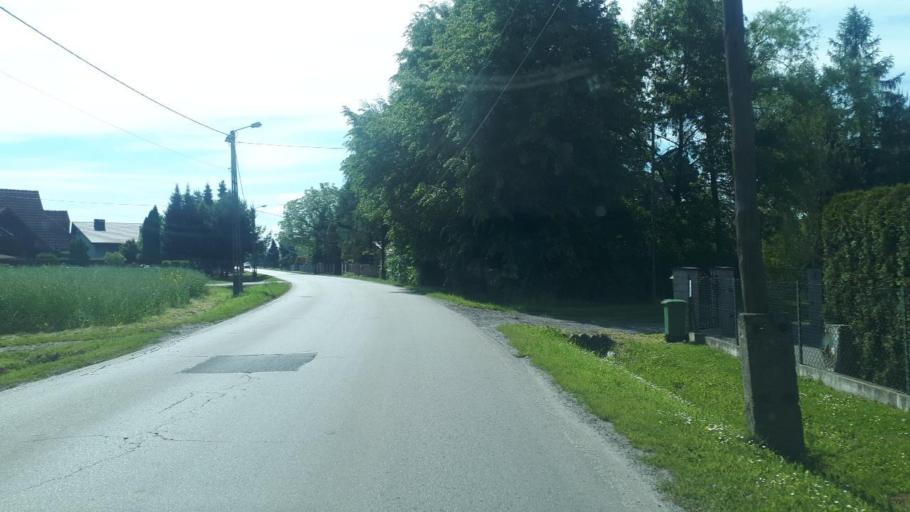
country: PL
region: Lesser Poland Voivodeship
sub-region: Powiat oswiecimski
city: Brzeszcze
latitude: 49.9539
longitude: 19.1395
